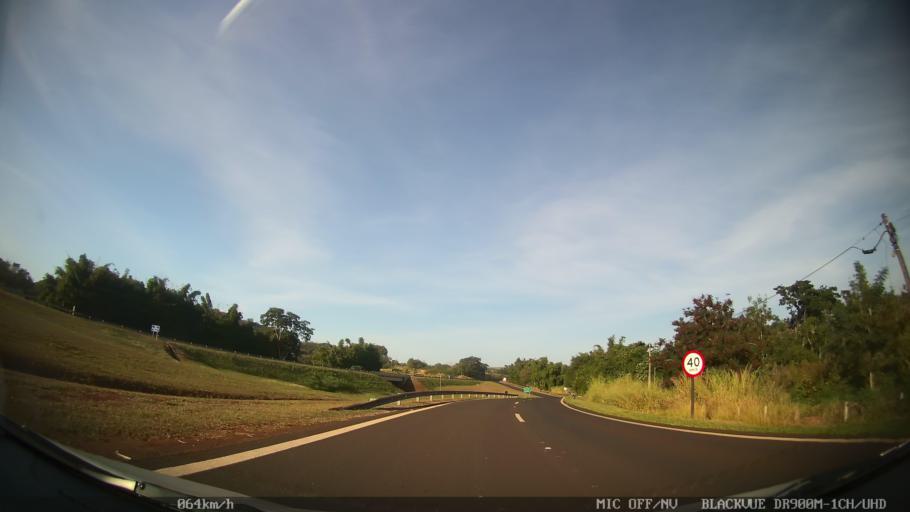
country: BR
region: Sao Paulo
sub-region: Cravinhos
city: Cravinhos
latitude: -21.2900
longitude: -47.8123
